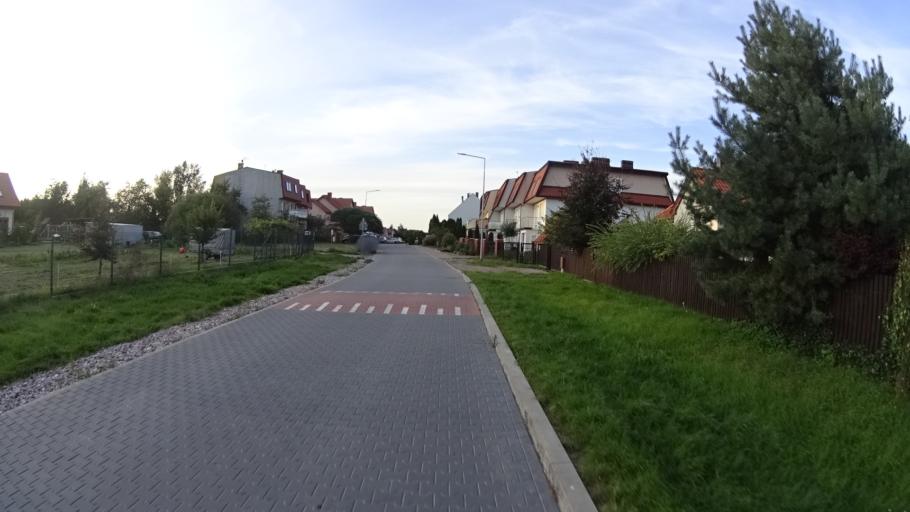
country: PL
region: Masovian Voivodeship
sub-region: Powiat legionowski
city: Nieporet
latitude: 52.4281
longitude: 21.0248
